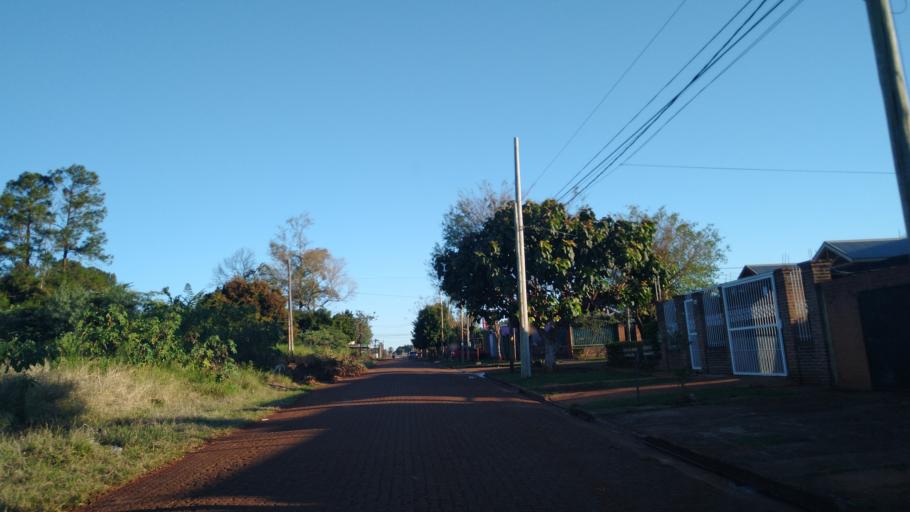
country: AR
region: Misiones
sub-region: Departamento de Capital
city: Posadas
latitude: -27.4075
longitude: -55.9497
